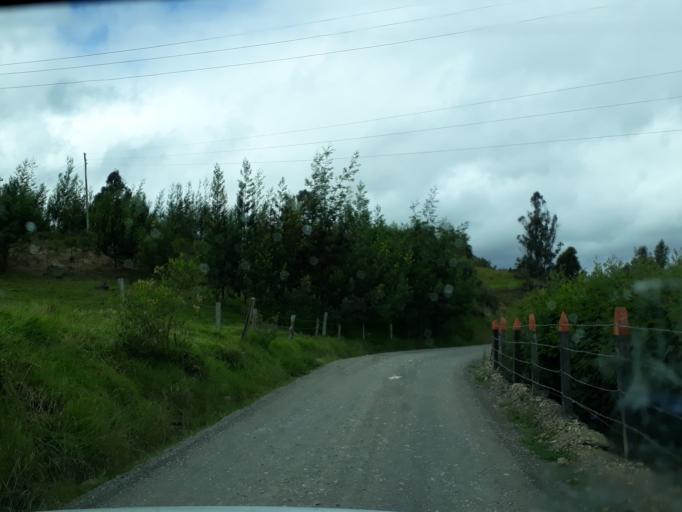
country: CO
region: Cundinamarca
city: Carmen de Carupa
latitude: 5.3198
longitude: -73.8897
